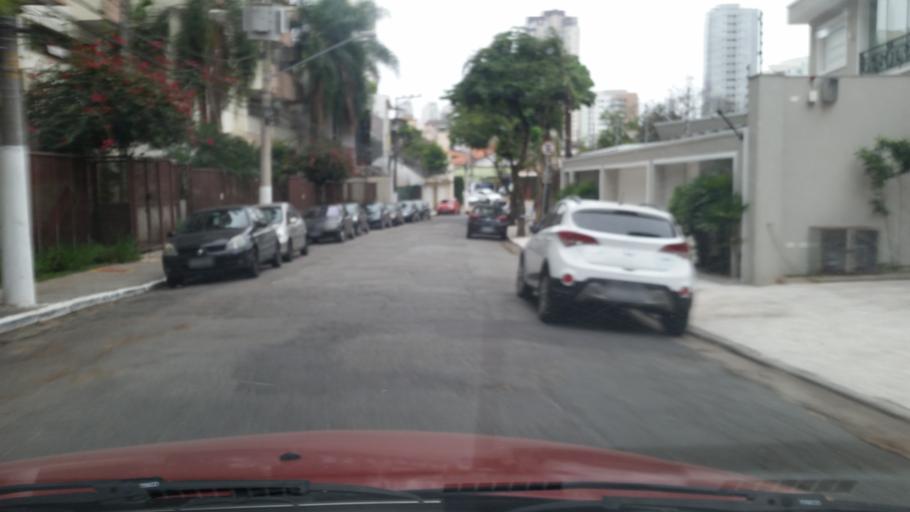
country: BR
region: Sao Paulo
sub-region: Sao Paulo
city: Sao Paulo
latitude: -23.5951
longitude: -46.6330
